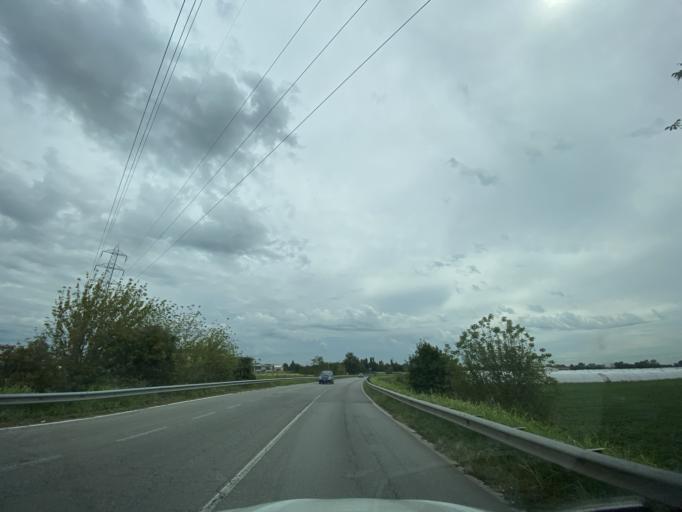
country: IT
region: Lombardy
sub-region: Provincia di Monza e Brianza
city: Agrate Brianza
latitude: 45.5649
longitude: 9.3523
